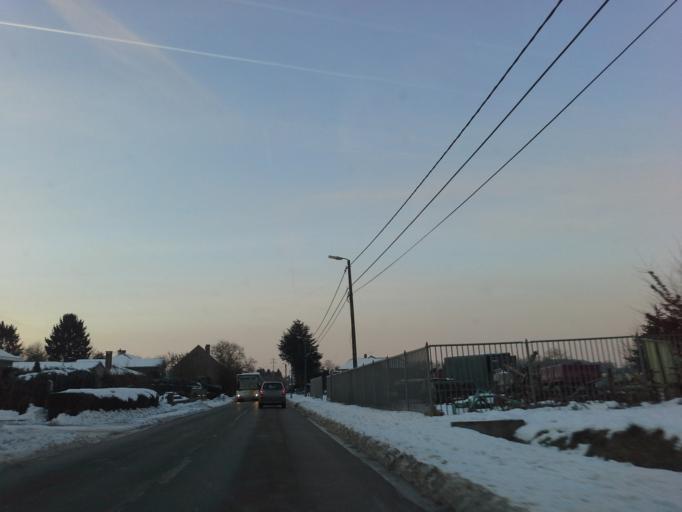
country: BE
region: Flanders
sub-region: Provincie Vlaams-Brabant
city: Lubbeek
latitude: 50.8780
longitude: 4.7948
